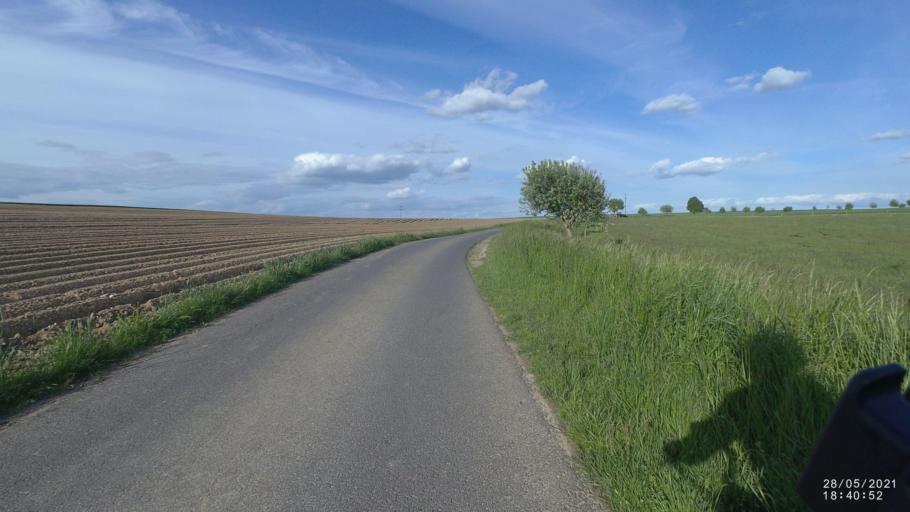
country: DE
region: Rheinland-Pfalz
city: Wierschem
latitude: 50.2293
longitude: 7.3558
